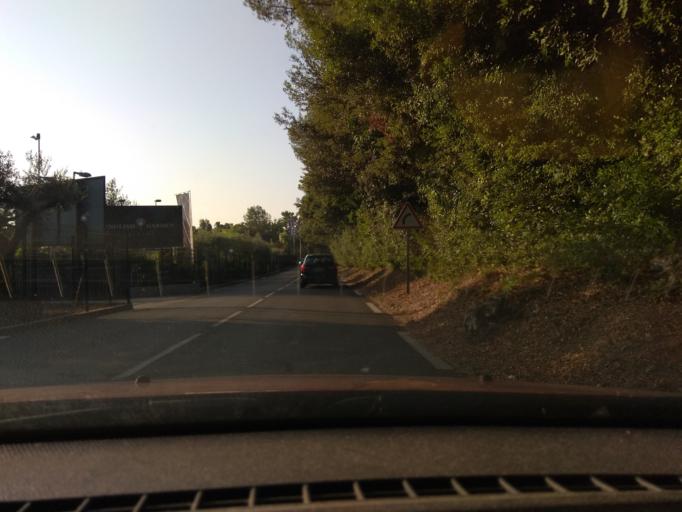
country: FR
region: Provence-Alpes-Cote d'Azur
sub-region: Departement des Alpes-Maritimes
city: Le Rouret
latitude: 43.6538
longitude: 7.0280
